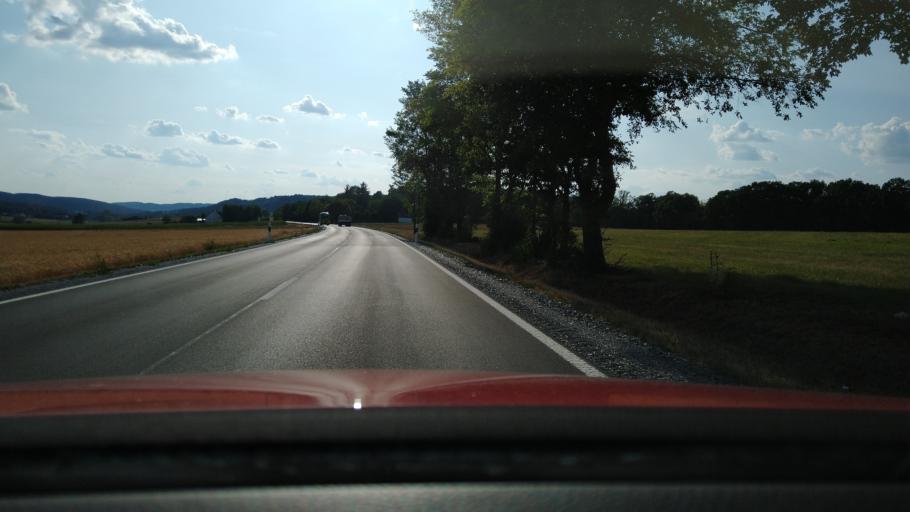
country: DE
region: Bavaria
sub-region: Upper Franconia
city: Mistelgau
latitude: 49.9293
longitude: 11.4696
